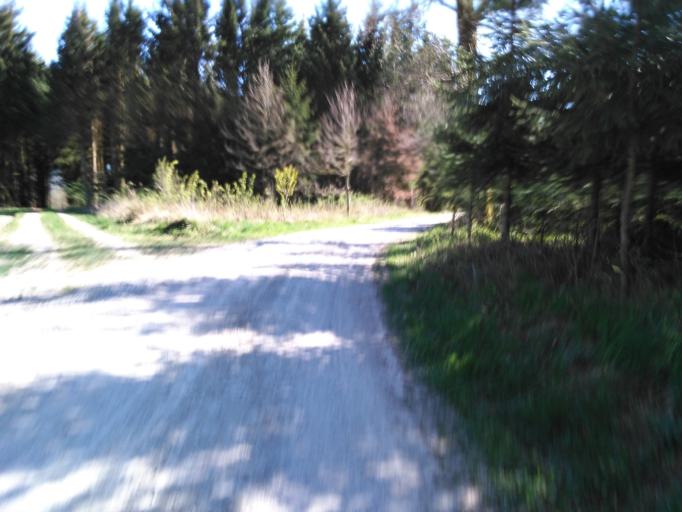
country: DE
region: Bavaria
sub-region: Upper Bavaria
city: Landsberied
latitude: 48.1995
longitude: 11.2044
